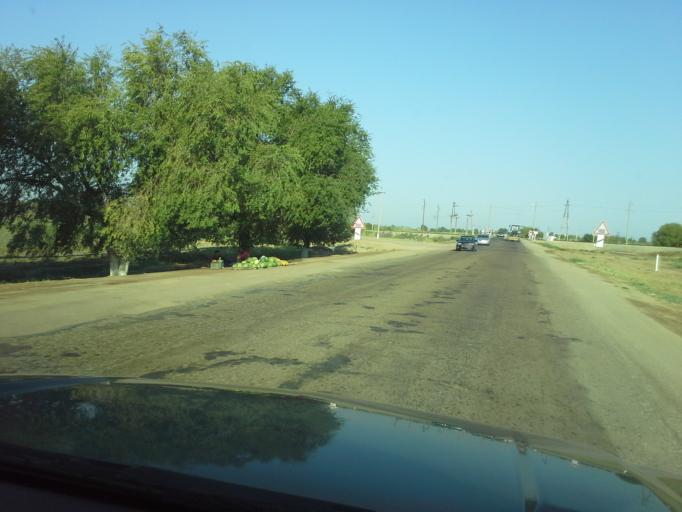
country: UZ
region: Karakalpakstan
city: Khujayli
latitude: 42.2302
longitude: 59.4659
